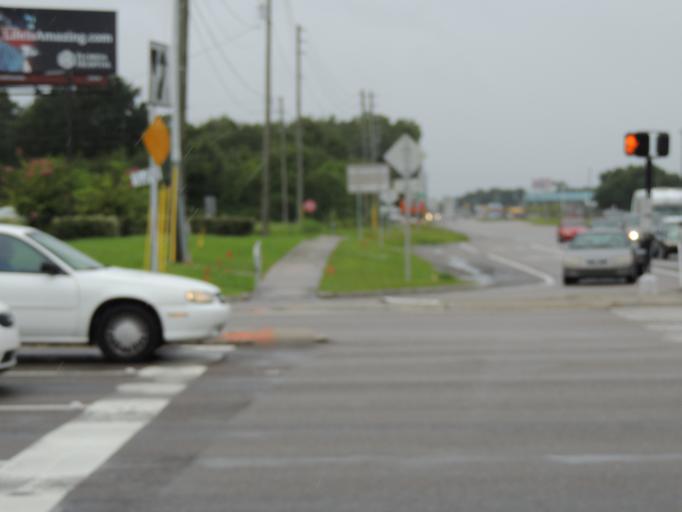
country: US
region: Florida
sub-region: Orange County
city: Hunters Creek
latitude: 28.3393
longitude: -81.4045
